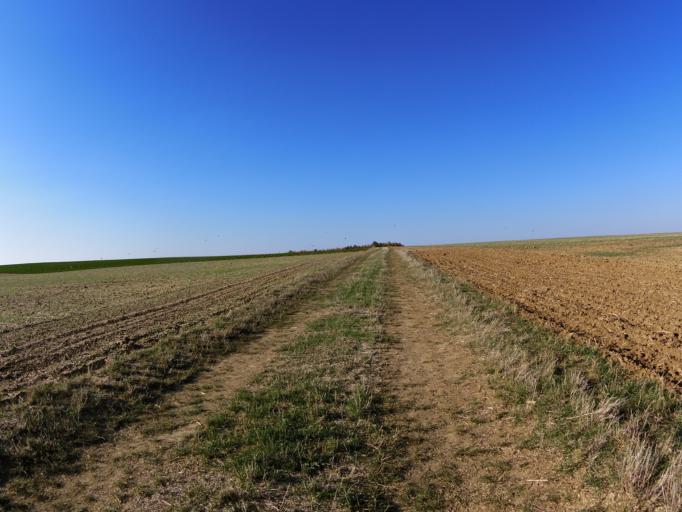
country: DE
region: Bavaria
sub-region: Regierungsbezirk Unterfranken
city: Eibelstadt
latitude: 49.7034
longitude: 9.9861
